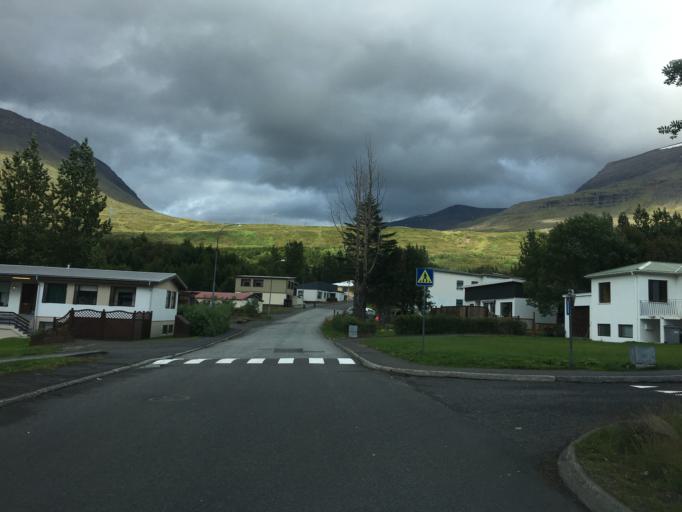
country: IS
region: East
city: Reydarfjoerdur
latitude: 65.0341
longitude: -14.2165
